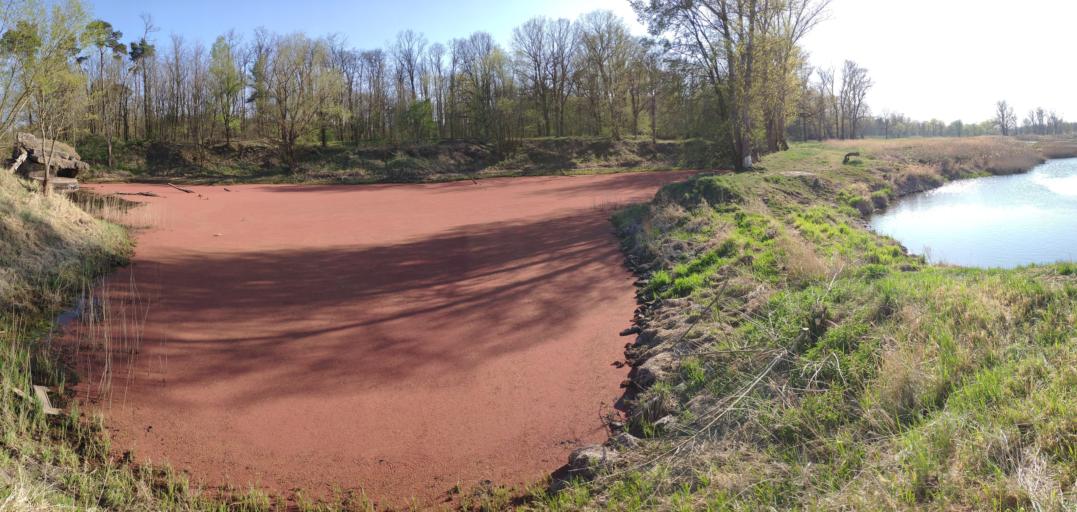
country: PL
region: Lubusz
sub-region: Powiat zielonogorski
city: Zabor
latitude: 51.9712
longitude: 15.7273
